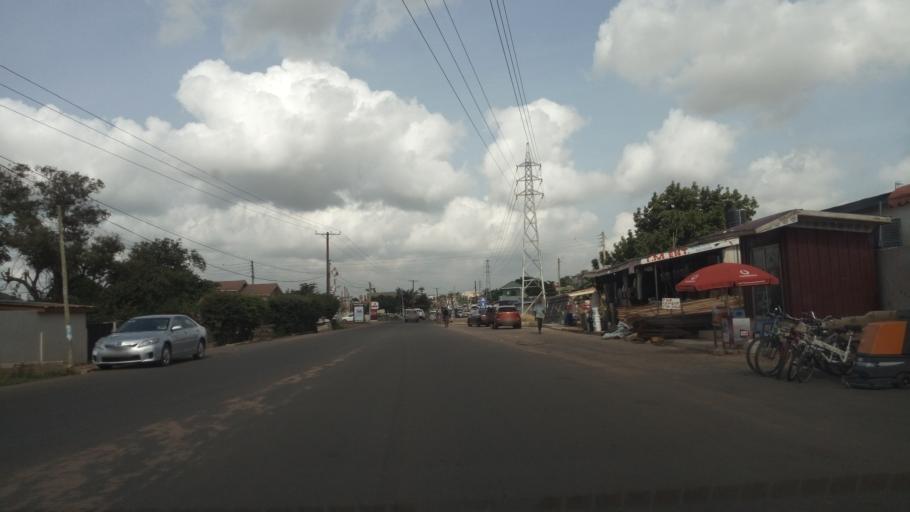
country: GH
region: Greater Accra
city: Medina Estates
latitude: 5.6599
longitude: -0.1521
